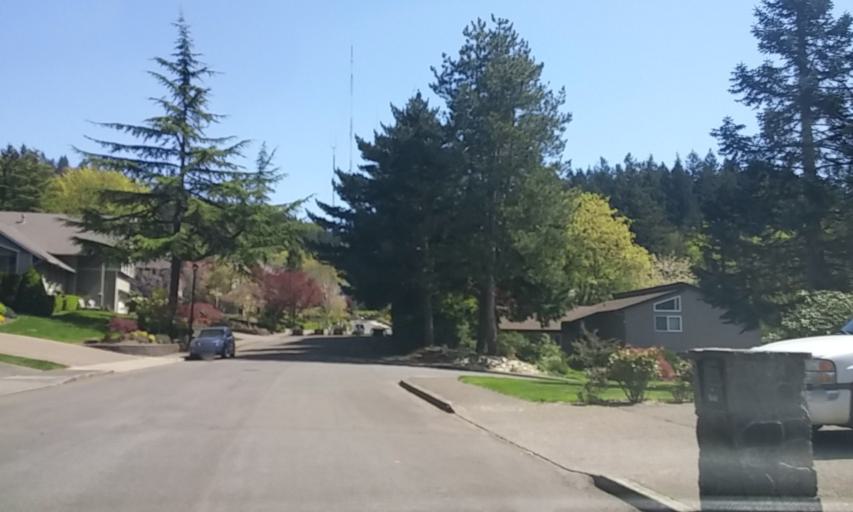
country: US
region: Oregon
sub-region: Washington County
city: West Haven
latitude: 45.5239
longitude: -122.7655
